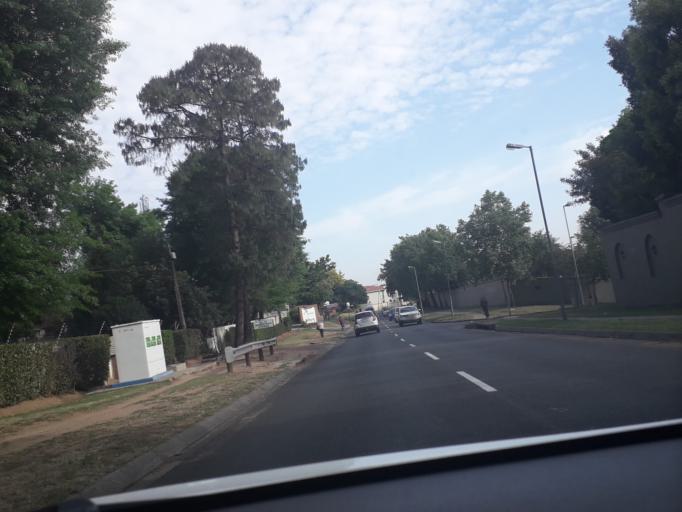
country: ZA
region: Gauteng
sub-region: City of Johannesburg Metropolitan Municipality
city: Diepsloot
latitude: -26.0675
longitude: 28.0011
